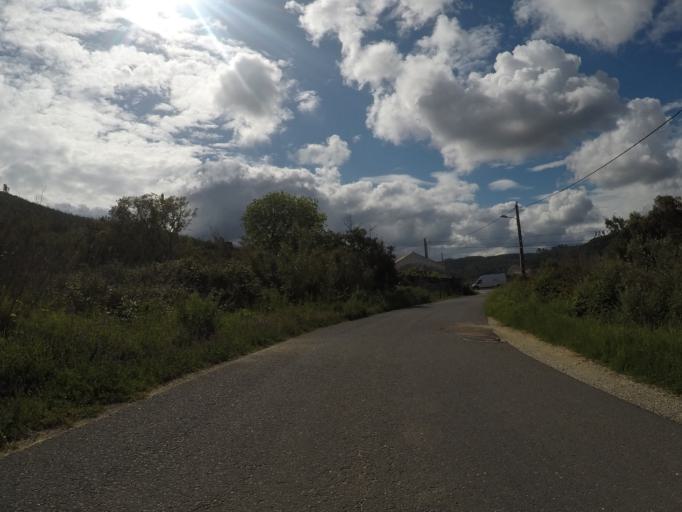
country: PT
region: Beja
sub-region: Odemira
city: Sao Teotonio
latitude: 37.4358
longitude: -8.7649
